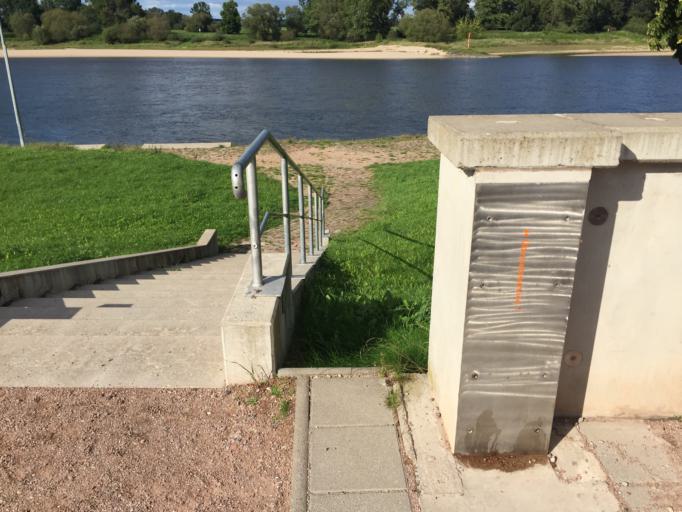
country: DE
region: Saxony-Anhalt
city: Dessau
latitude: 51.8565
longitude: 12.2171
